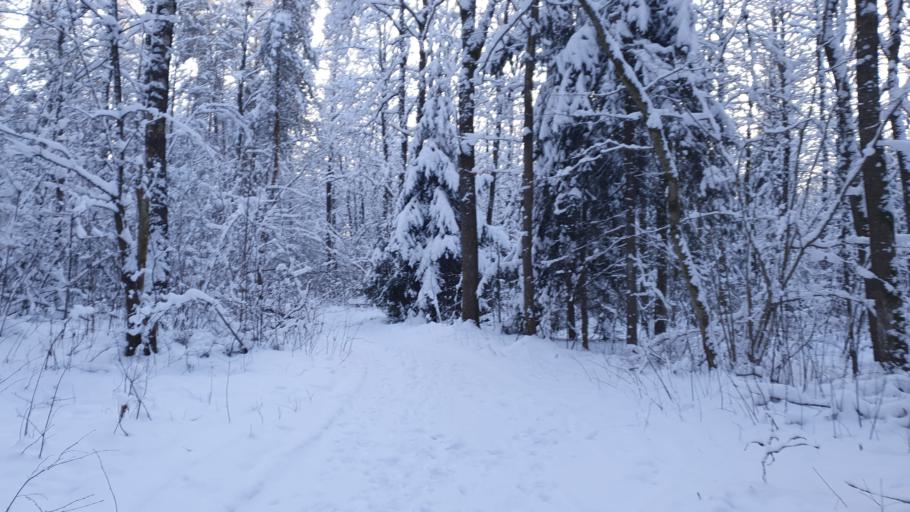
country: LT
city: Skaidiskes
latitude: 54.6441
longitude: 25.4175
